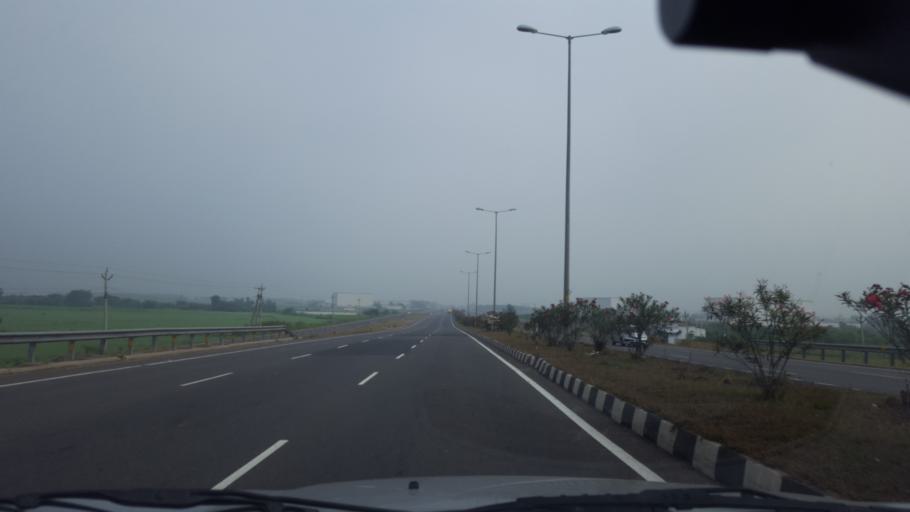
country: IN
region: Andhra Pradesh
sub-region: Guntur
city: Chilakalurupet
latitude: 16.0325
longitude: 80.1308
